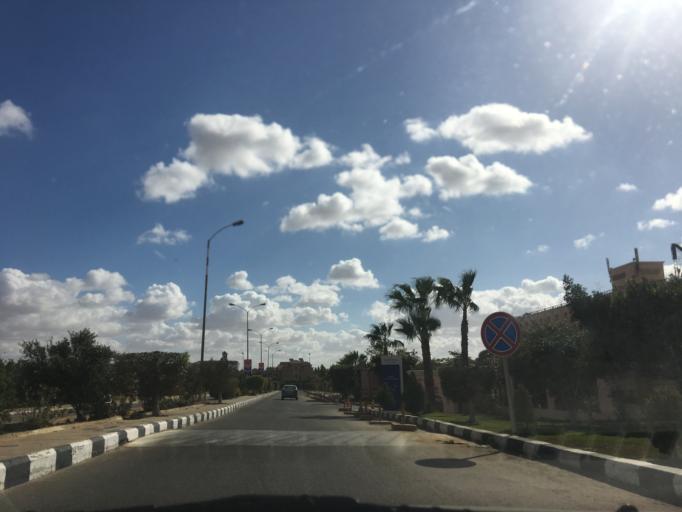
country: EG
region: Al Jizah
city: Madinat Sittah Uktubar
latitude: 29.9975
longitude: 30.9690
